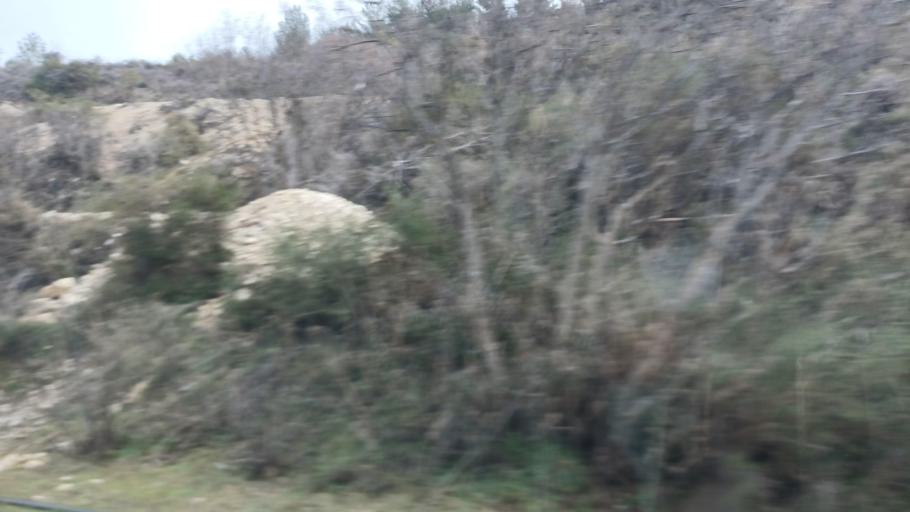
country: CY
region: Limassol
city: Pachna
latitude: 34.8686
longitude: 32.7658
